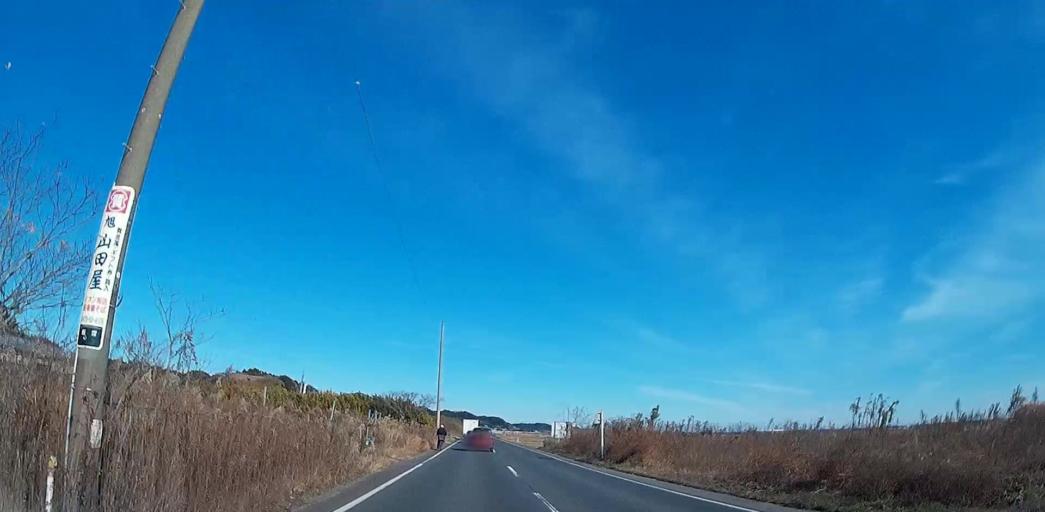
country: JP
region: Chiba
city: Yokaichiba
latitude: 35.7419
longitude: 140.5638
